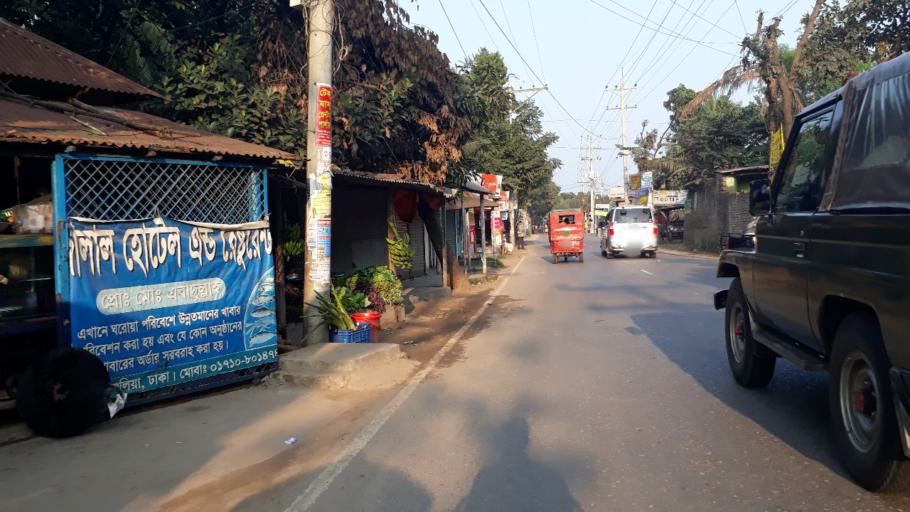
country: BD
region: Dhaka
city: Tungi
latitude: 23.8804
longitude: 90.2979
